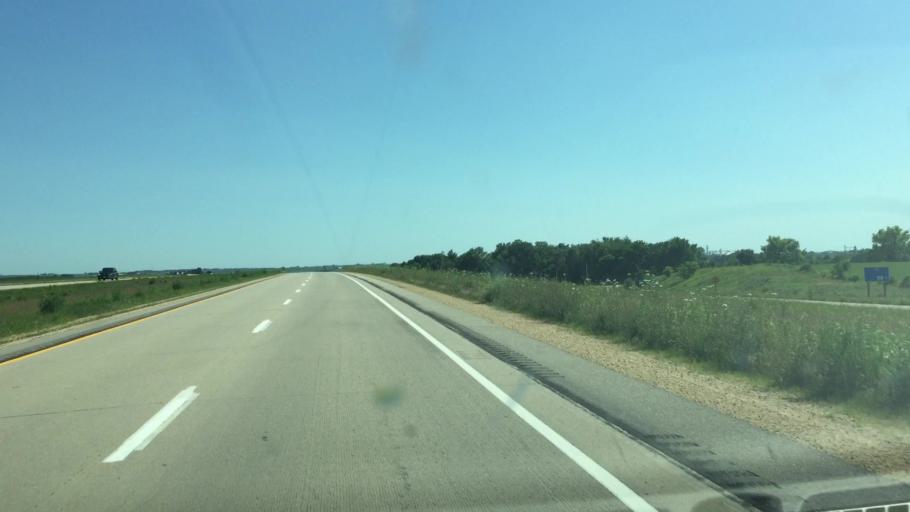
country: US
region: Iowa
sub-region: Jones County
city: Monticello
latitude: 42.2335
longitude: -91.1706
